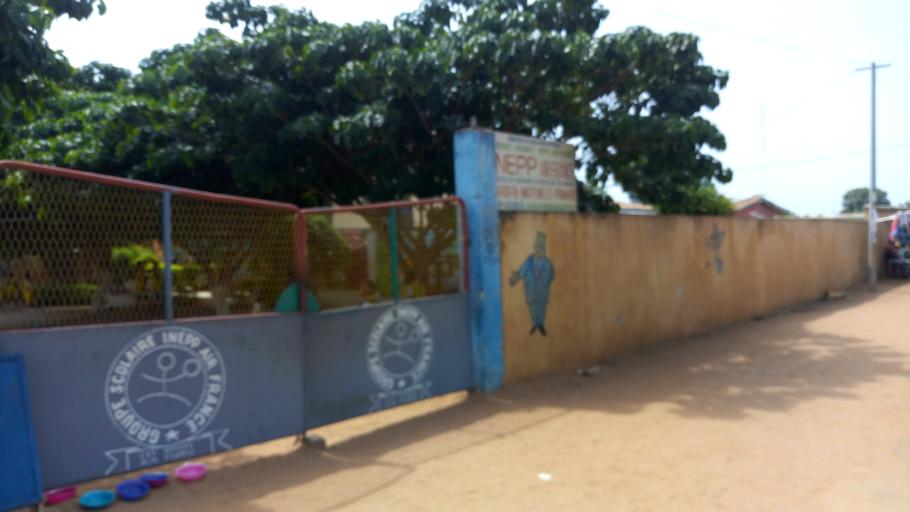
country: CI
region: Vallee du Bandama
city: Bouake
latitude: 7.6709
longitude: -5.0139
